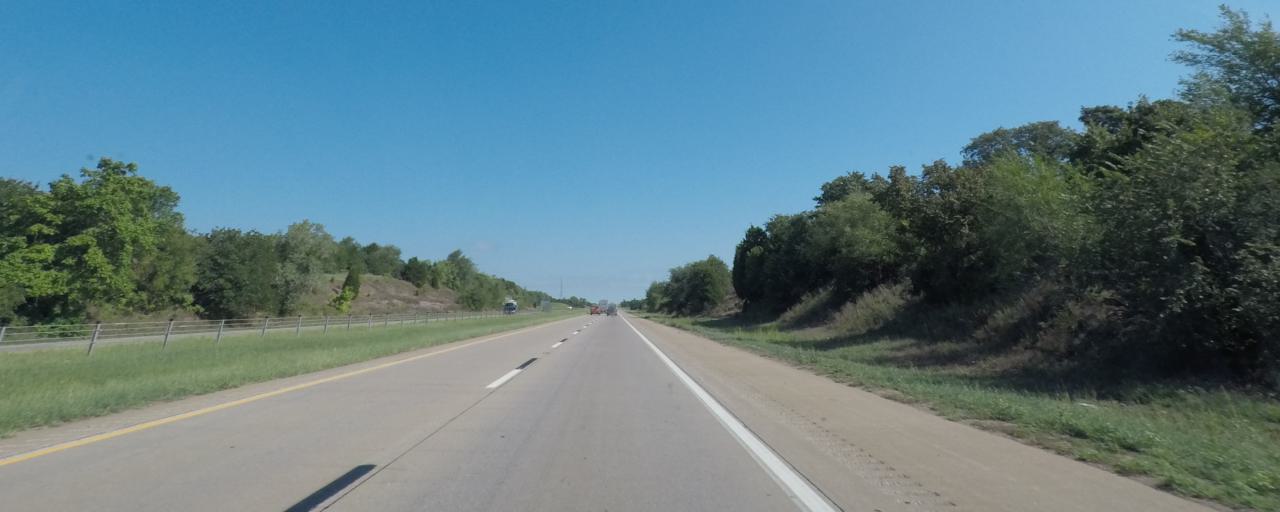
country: US
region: Oklahoma
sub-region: Oklahoma County
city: Edmond
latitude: 35.7402
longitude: -97.4162
